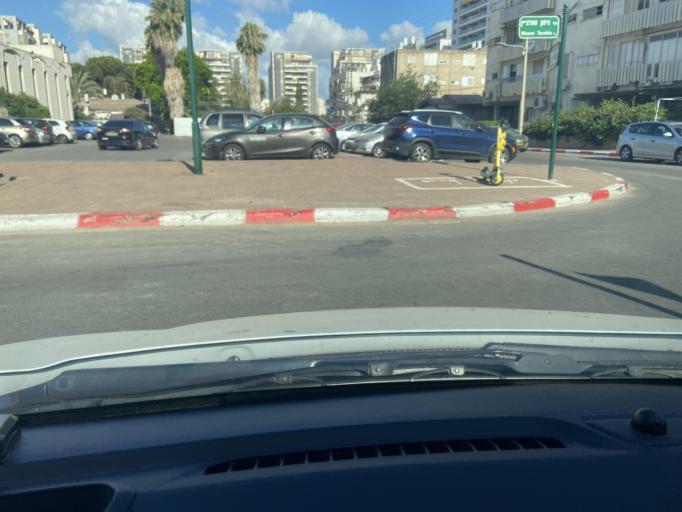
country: IL
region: Central District
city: Yehud
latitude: 32.0313
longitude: 34.8897
